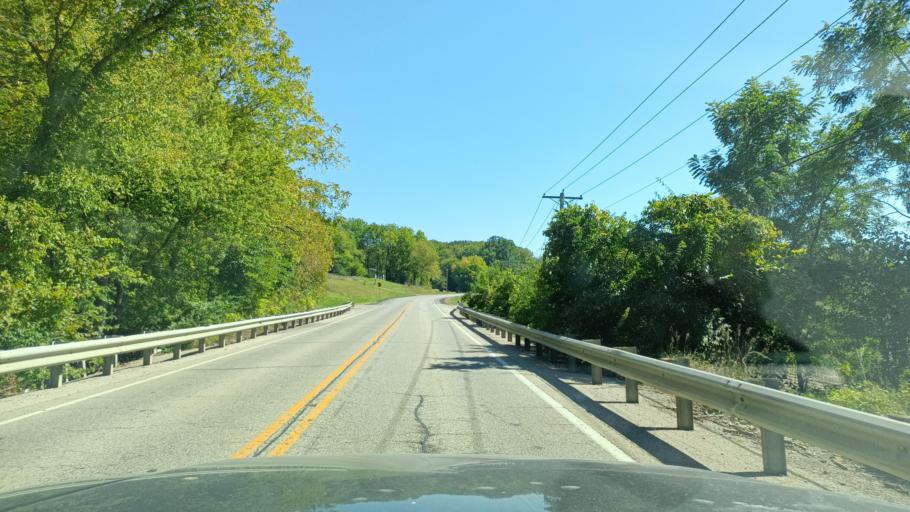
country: US
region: Illinois
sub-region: Woodford County
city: Eureka
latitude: 40.6263
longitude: -89.2462
